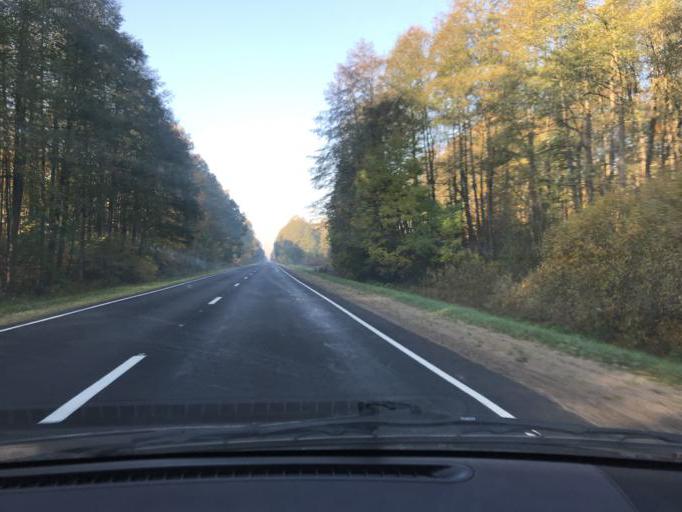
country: BY
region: Brest
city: Baranovichi
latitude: 52.8883
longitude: 25.8090
